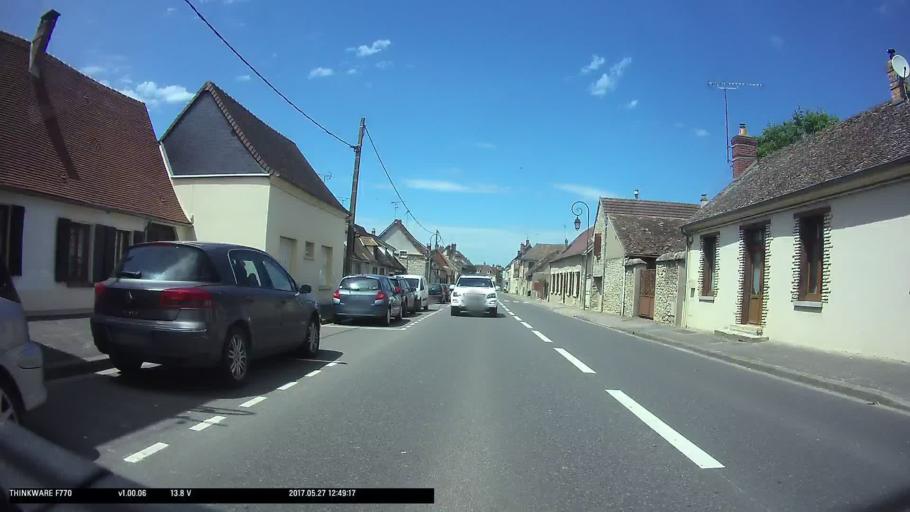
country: FR
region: Picardie
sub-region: Departement de l'Oise
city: Trie-Chateau
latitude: 49.2826
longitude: 1.8258
